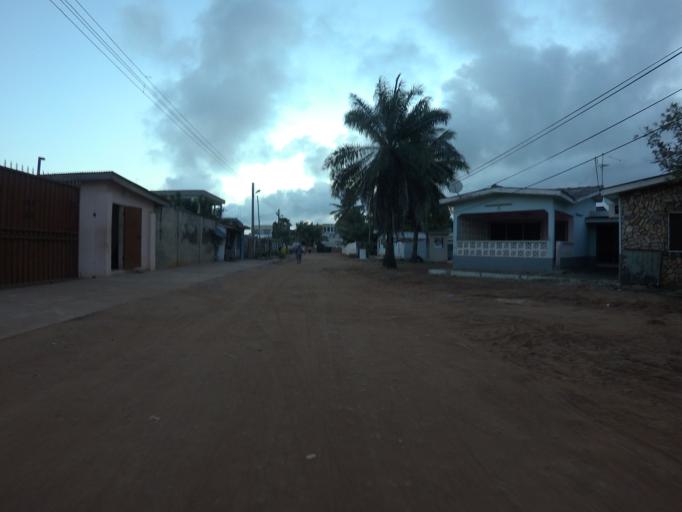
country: GH
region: Greater Accra
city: Accra
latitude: 5.5599
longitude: -0.1724
